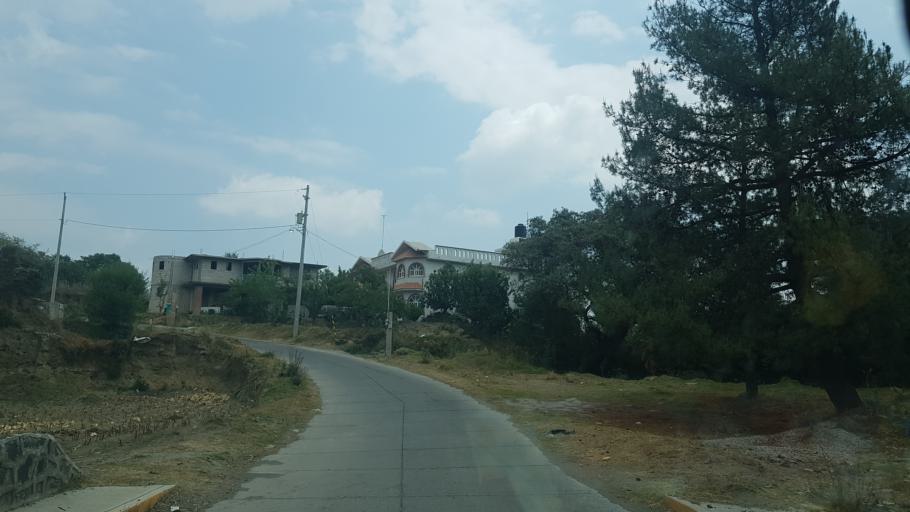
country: MX
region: Puebla
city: Domingo Arenas
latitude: 19.1393
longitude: -98.4767
